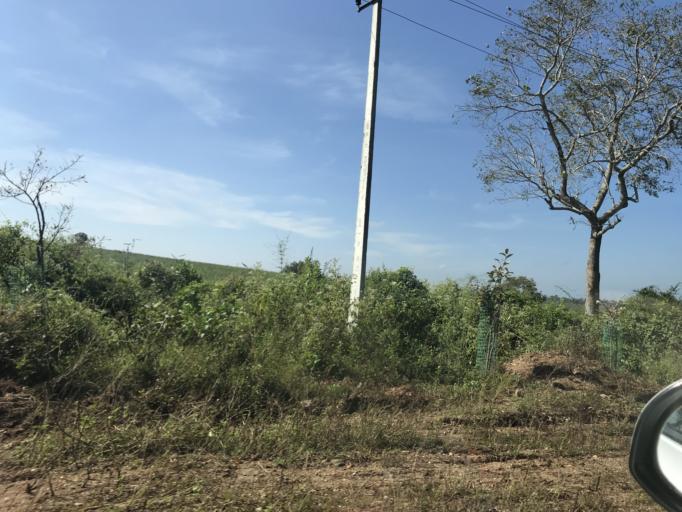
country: IN
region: Karnataka
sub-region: Mysore
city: Heggadadevankote
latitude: 12.0153
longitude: 76.2681
